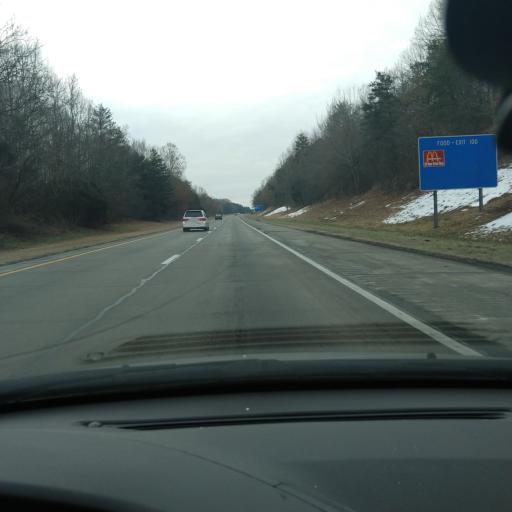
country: US
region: North Carolina
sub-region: Davidson County
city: Midway
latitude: 35.9809
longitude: -80.2338
